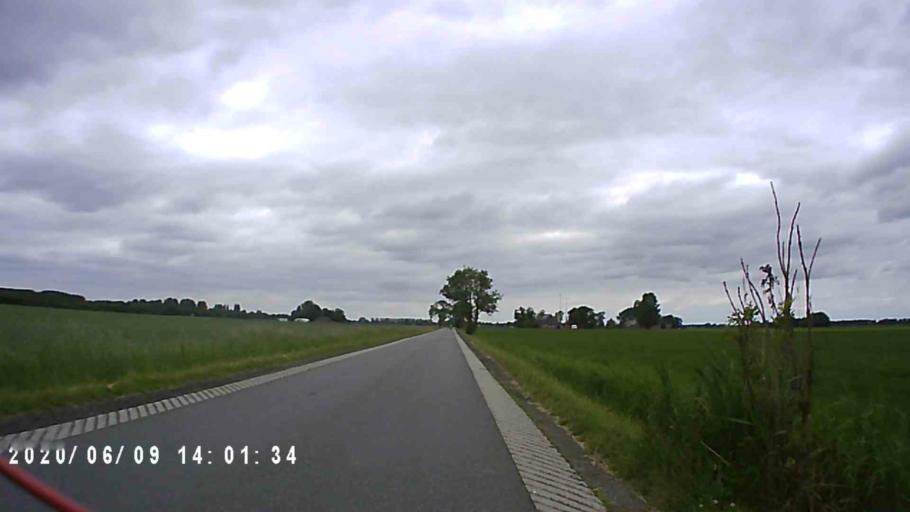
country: NL
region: Groningen
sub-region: Gemeente Bedum
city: Bedum
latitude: 53.2570
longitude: 6.6202
